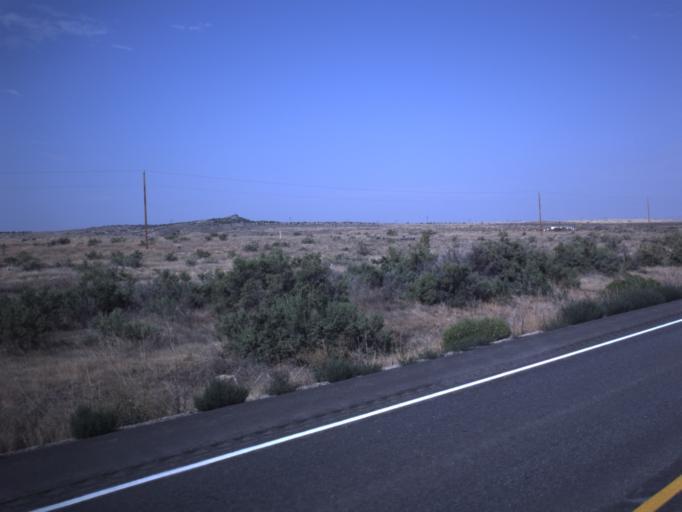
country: US
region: Utah
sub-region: Uintah County
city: Naples
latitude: 40.3046
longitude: -109.2054
